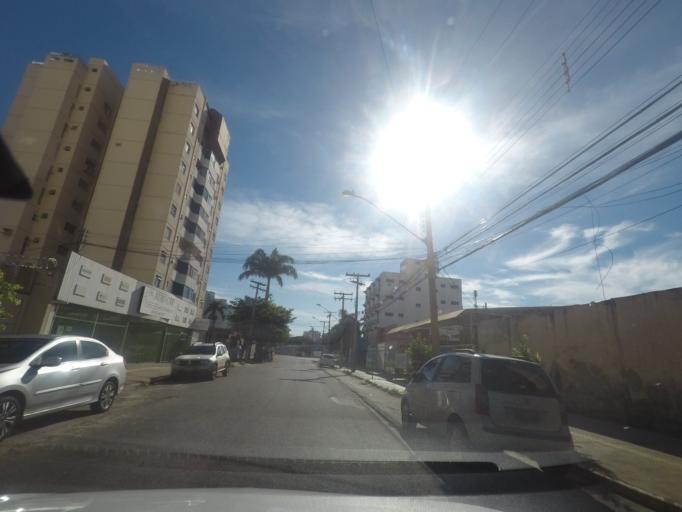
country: BR
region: Goias
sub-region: Goiania
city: Goiania
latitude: -16.6731
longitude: -49.2702
